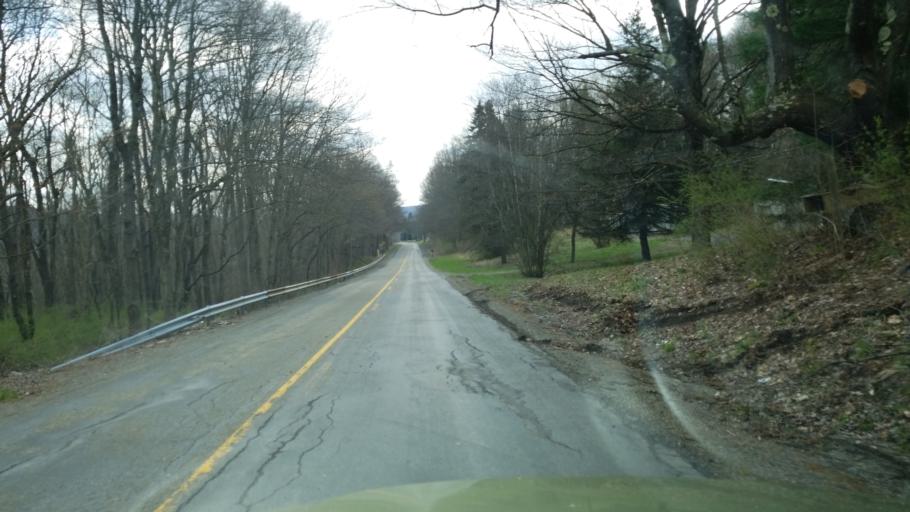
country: US
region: Pennsylvania
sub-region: Jefferson County
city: Brockway
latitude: 41.2726
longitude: -78.8193
